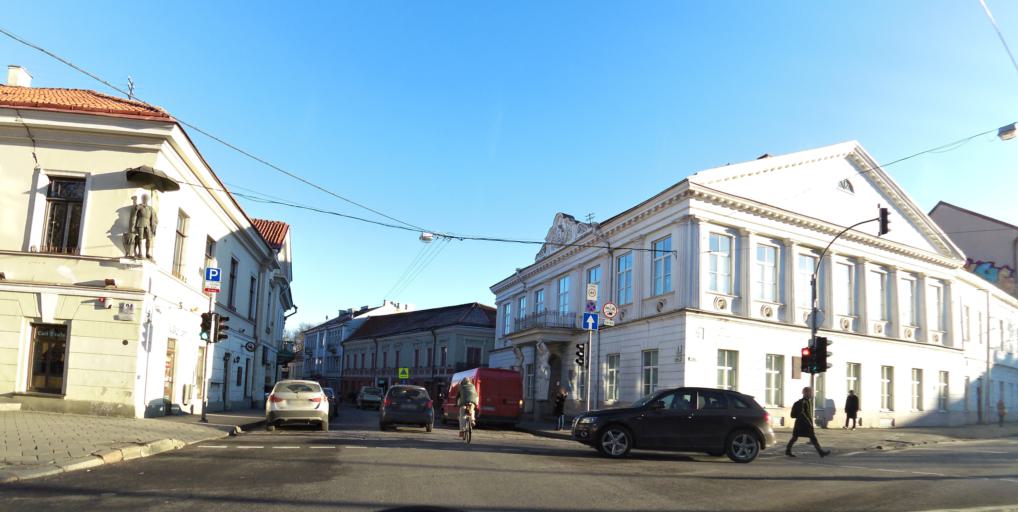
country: LT
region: Vilnius County
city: Naujamiestis
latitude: 54.6799
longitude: 25.2779
